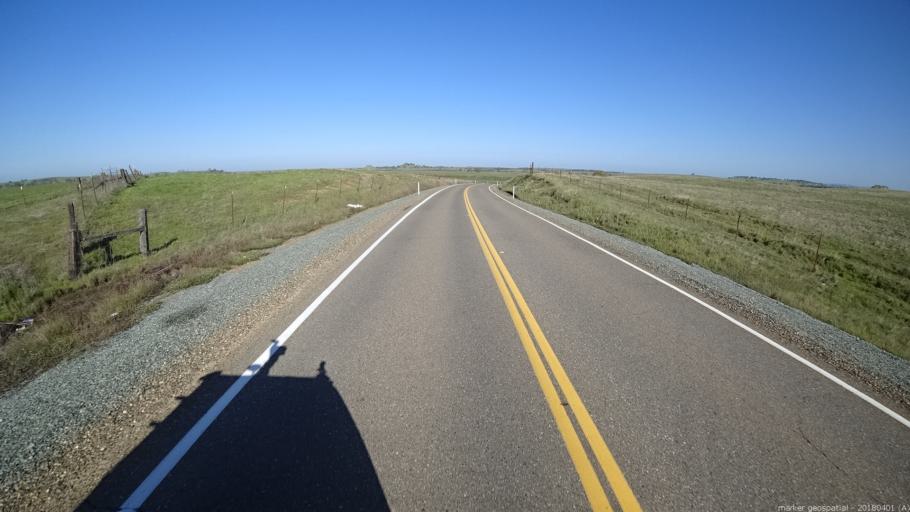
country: US
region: California
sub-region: Sacramento County
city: Rancho Murieta
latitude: 38.4130
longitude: -121.0363
